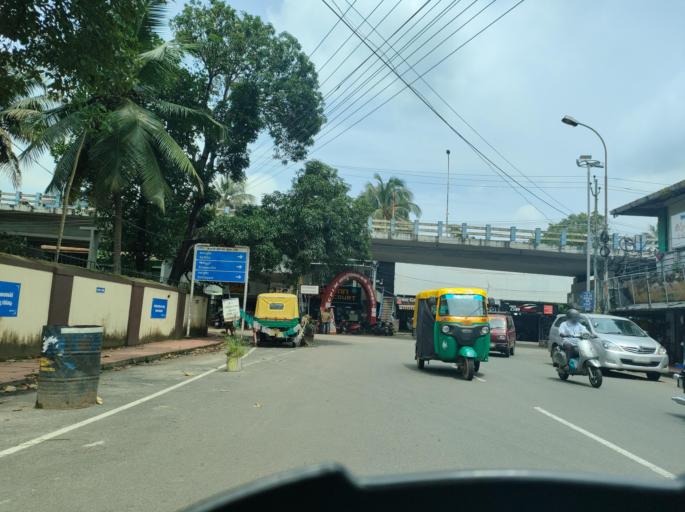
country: IN
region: Kerala
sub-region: Ernakulam
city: Cochin
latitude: 9.9746
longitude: 76.3152
